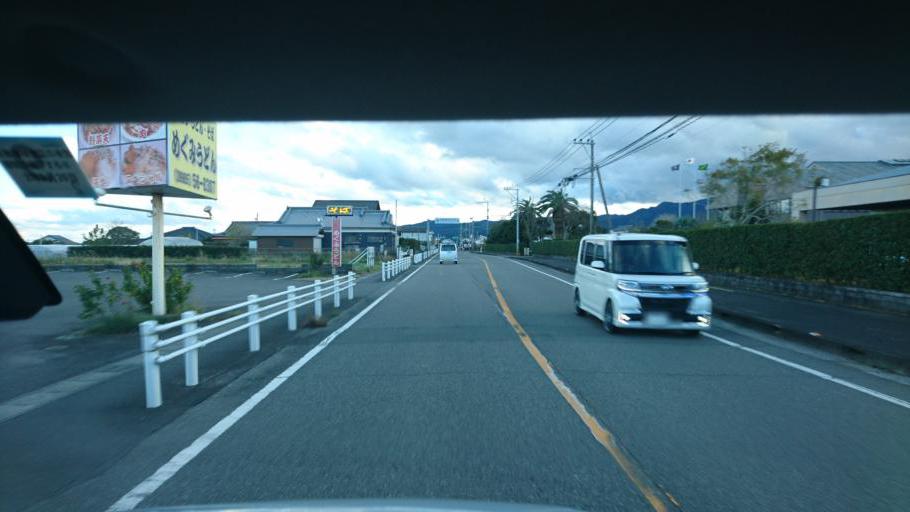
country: JP
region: Miyazaki
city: Miyazaki-shi
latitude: 31.8502
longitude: 131.4353
